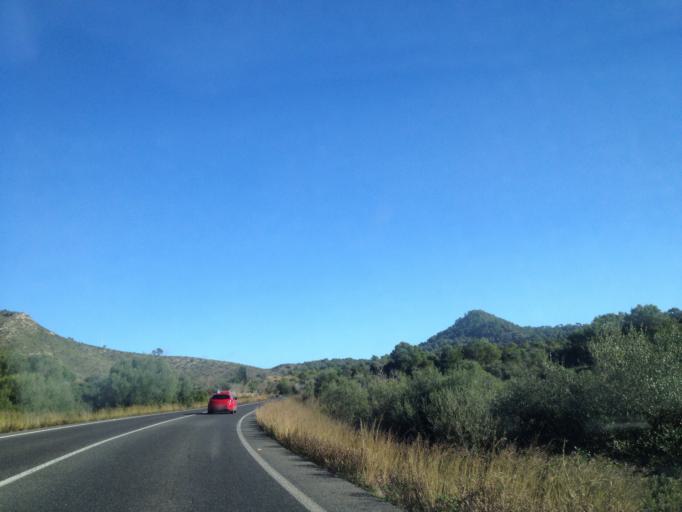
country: ES
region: Balearic Islands
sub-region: Illes Balears
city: Sant Llorenc des Cardassar
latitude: 39.6357
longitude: 3.3029
